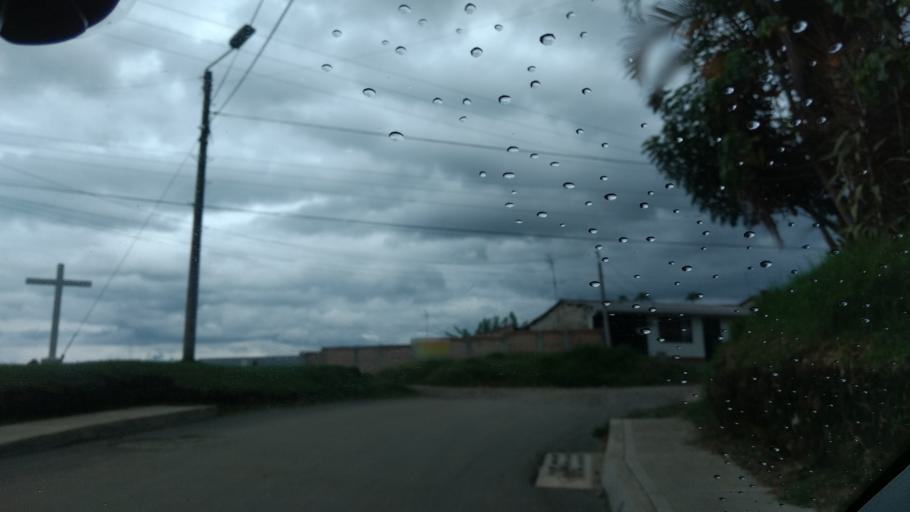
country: CO
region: Cauca
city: Popayan
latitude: 2.4908
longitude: -76.5749
